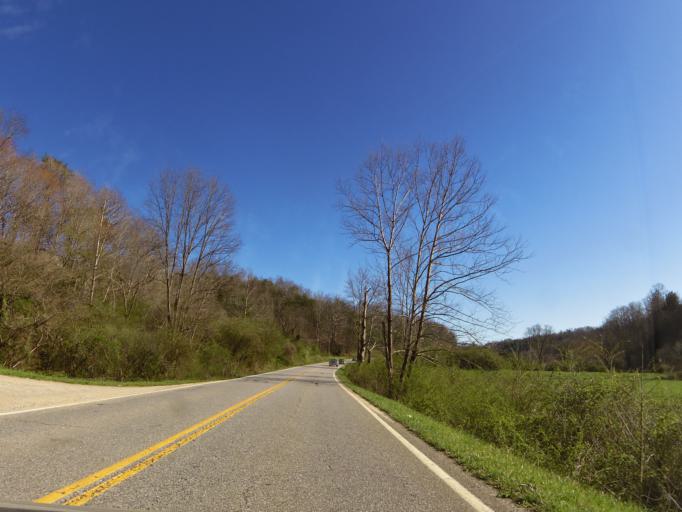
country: US
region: Tennessee
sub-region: Scott County
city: Oneida
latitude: 36.4696
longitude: -84.4788
